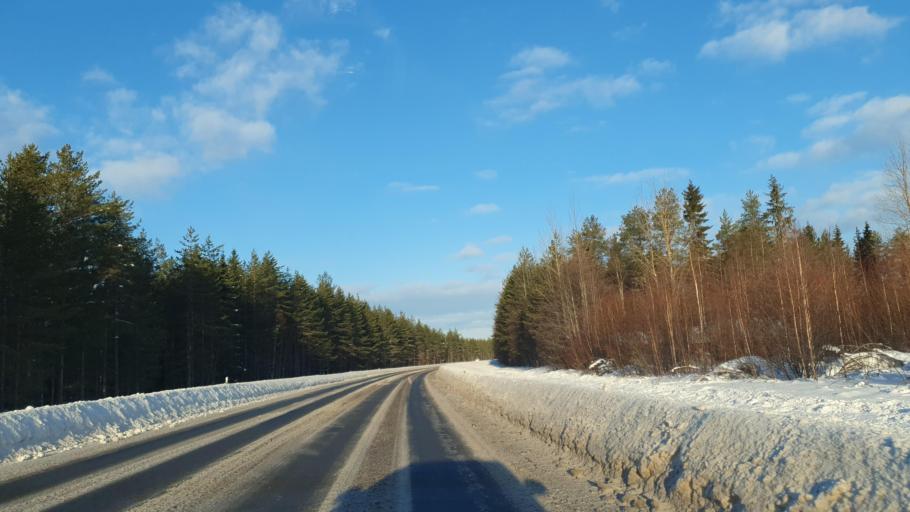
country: FI
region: Northern Ostrobothnia
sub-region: Oulunkaari
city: Utajaervi
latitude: 64.7268
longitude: 26.4896
